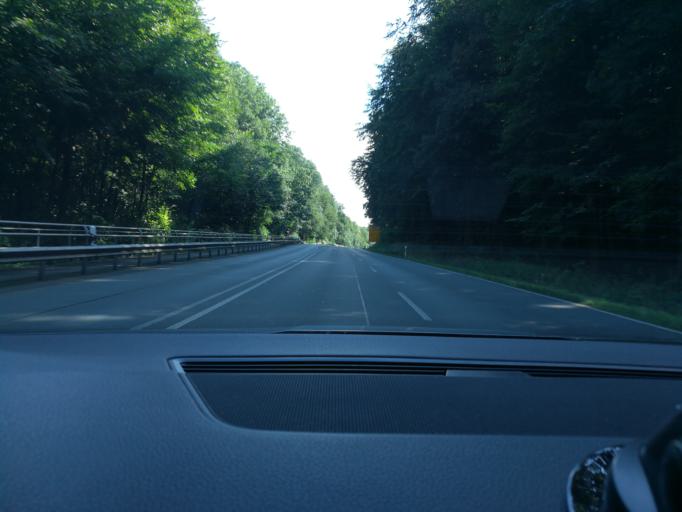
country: DE
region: North Rhine-Westphalia
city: Lubbecke
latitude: 52.2878
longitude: 8.6250
